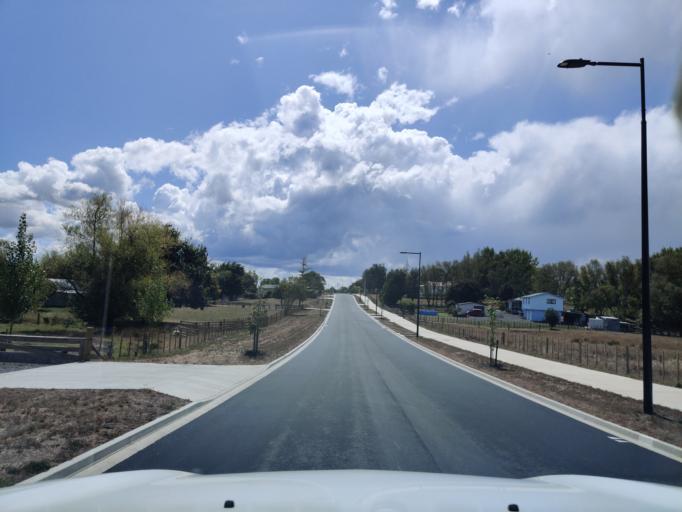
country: NZ
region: Waikato
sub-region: Waikato District
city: Te Kauwhata
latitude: -37.4099
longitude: 175.1454
